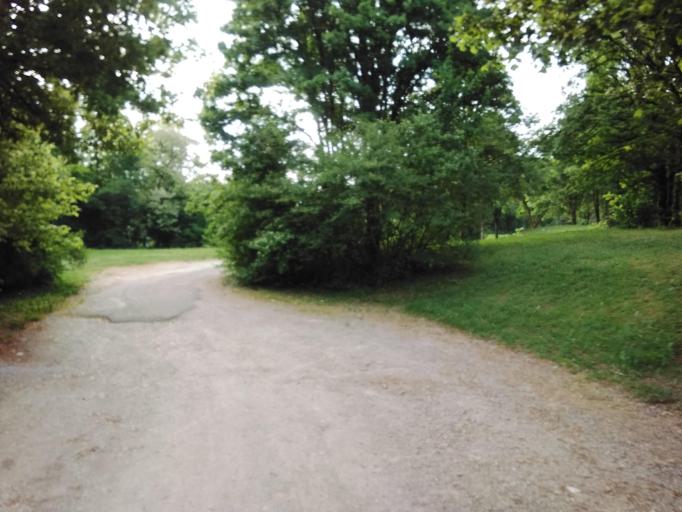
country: FR
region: Franche-Comte
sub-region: Departement du Jura
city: Arbois
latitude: 46.8981
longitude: 5.7911
